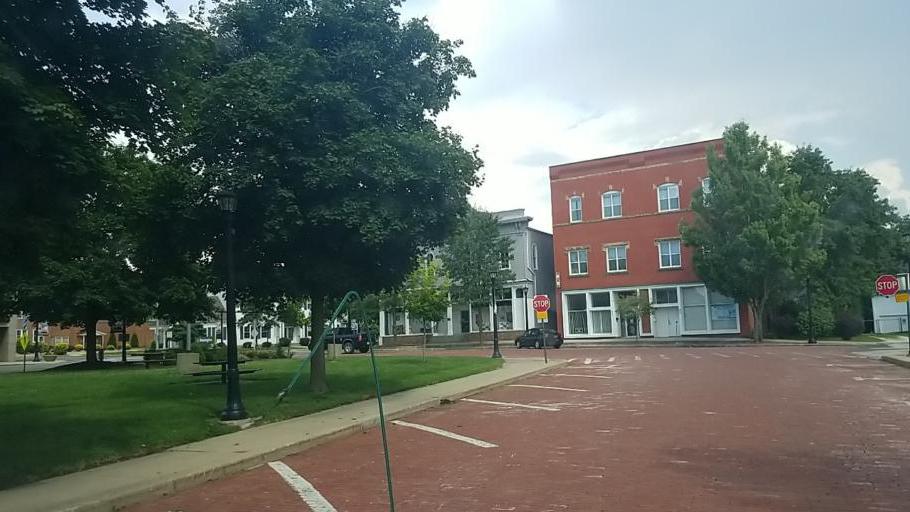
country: US
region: Ohio
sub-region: Medina County
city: Lodi
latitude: 41.0327
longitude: -82.0120
